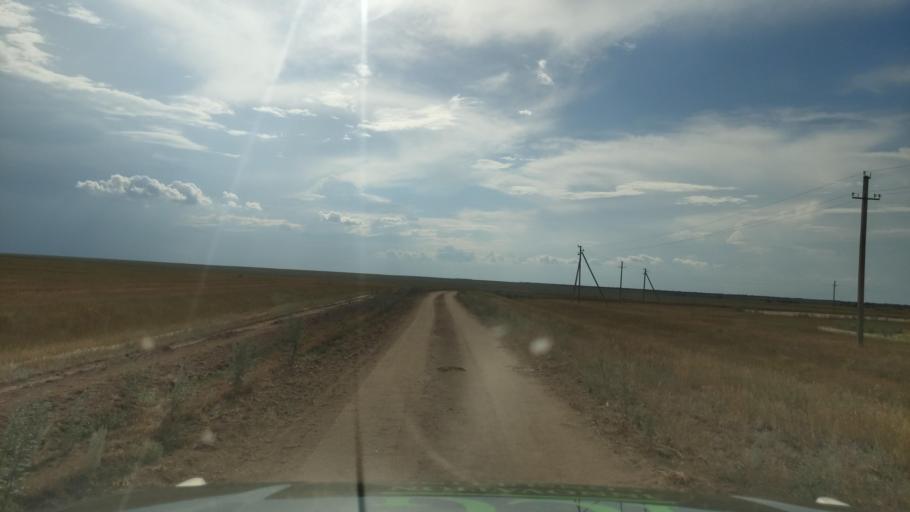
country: KZ
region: Pavlodar
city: Pavlodar
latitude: 52.5088
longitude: 77.5558
